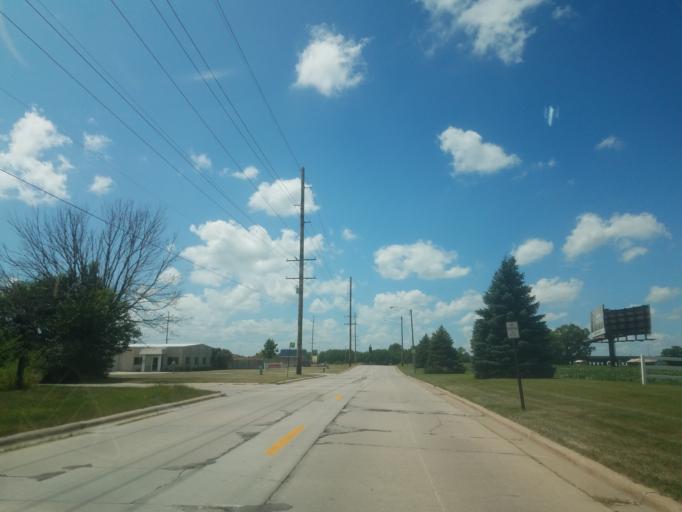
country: US
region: Illinois
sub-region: McLean County
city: Bloomington
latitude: 40.5024
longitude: -89.0240
